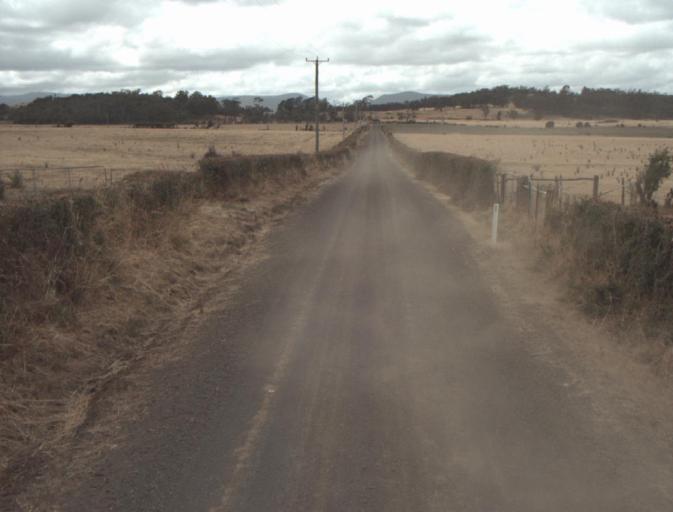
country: AU
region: Tasmania
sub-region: Northern Midlands
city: Evandale
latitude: -41.5202
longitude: 147.2853
